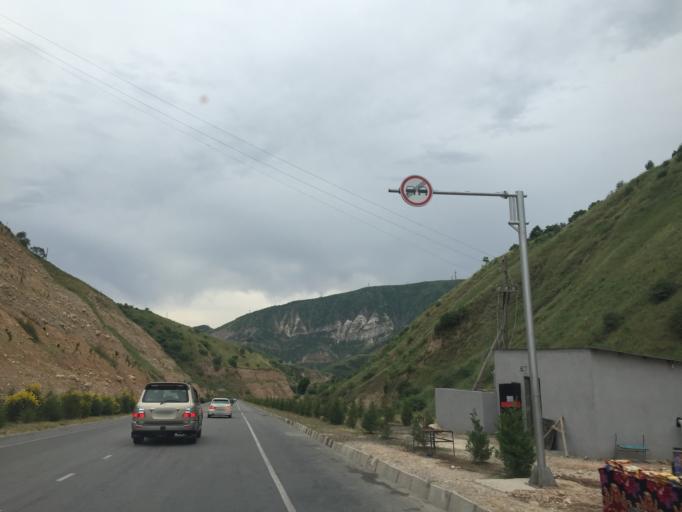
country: TJ
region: Khatlon
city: Norak
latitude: 38.4507
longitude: 69.2015
